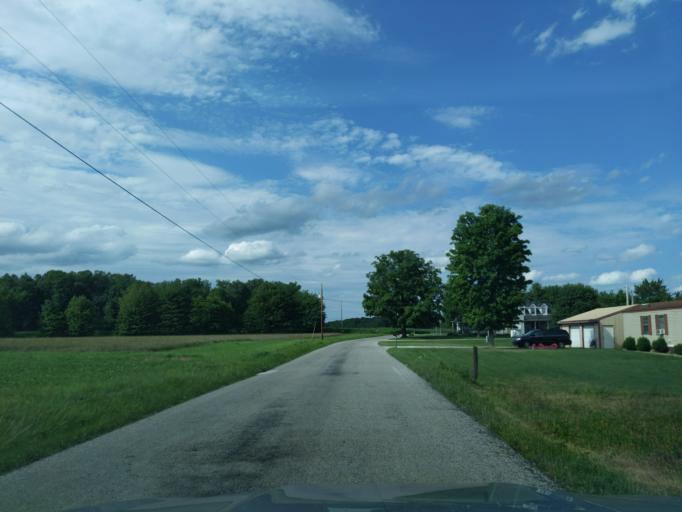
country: US
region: Indiana
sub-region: Ripley County
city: Sunman
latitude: 39.2982
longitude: -85.0893
